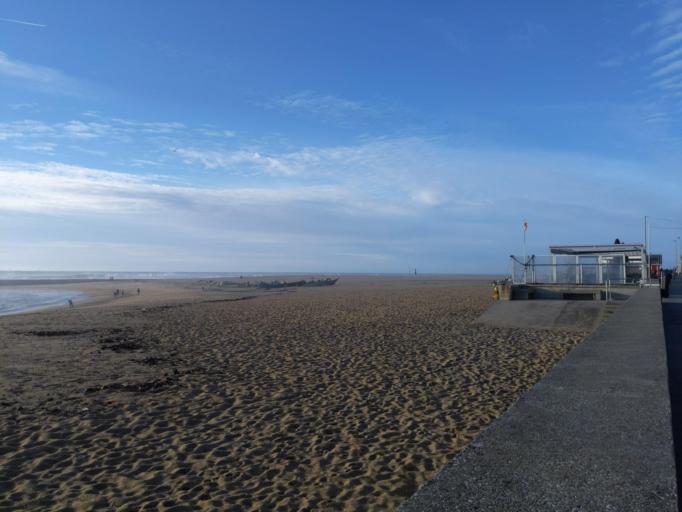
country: PT
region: Porto
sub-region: Vila Nova de Gaia
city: Arcozelo
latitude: 41.0484
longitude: -8.6539
